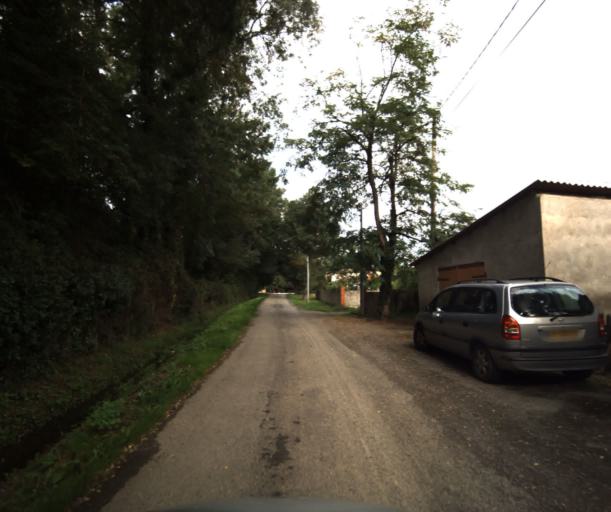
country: FR
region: Midi-Pyrenees
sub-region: Departement de la Haute-Garonne
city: Le Fauga
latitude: 43.4412
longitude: 1.2948
